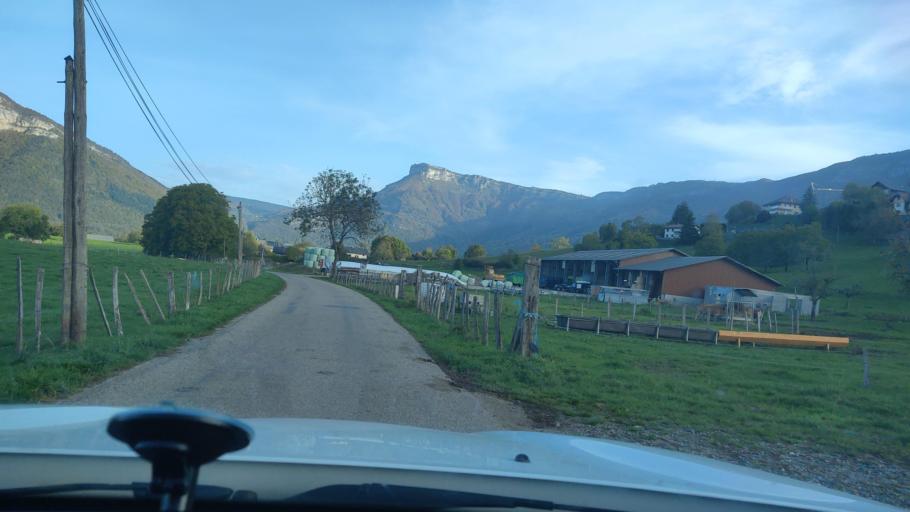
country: FR
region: Rhone-Alpes
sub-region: Departement de la Savoie
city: Barby
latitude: 45.5685
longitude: 6.0239
